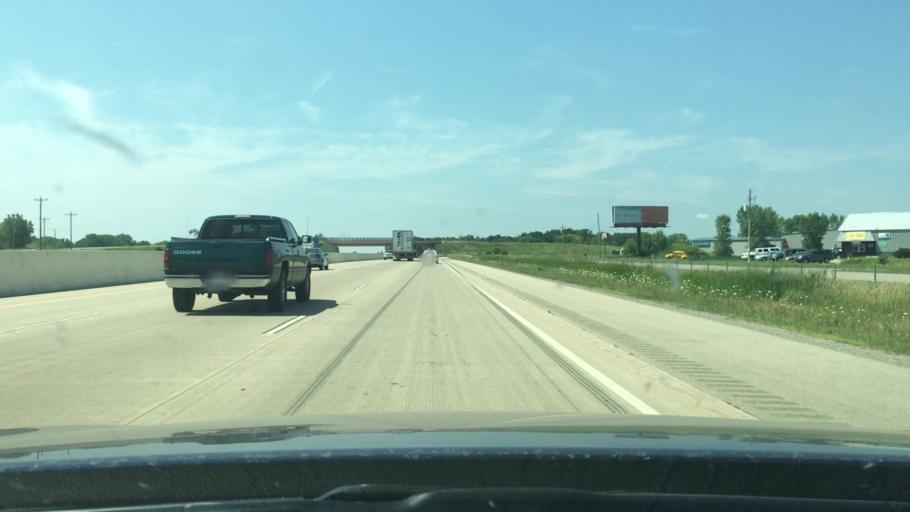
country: US
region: Wisconsin
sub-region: Winnebago County
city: Neenah
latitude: 44.1149
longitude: -88.5165
